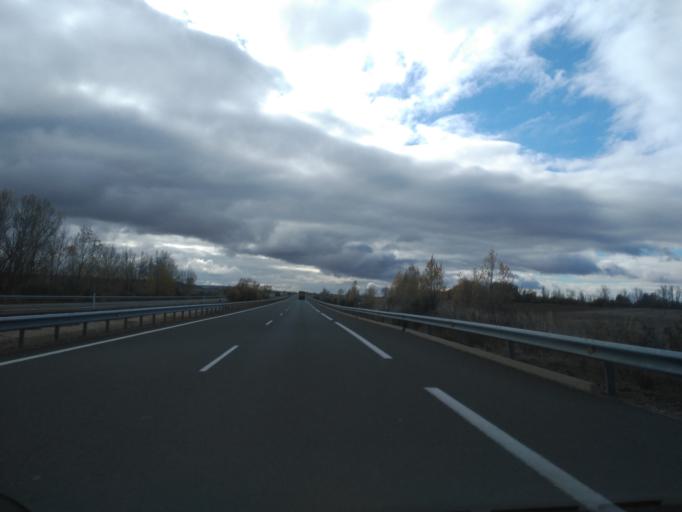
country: ES
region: Castille and Leon
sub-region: Provincia de Palencia
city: Pina de Campos
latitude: 42.2358
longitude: -4.4271
